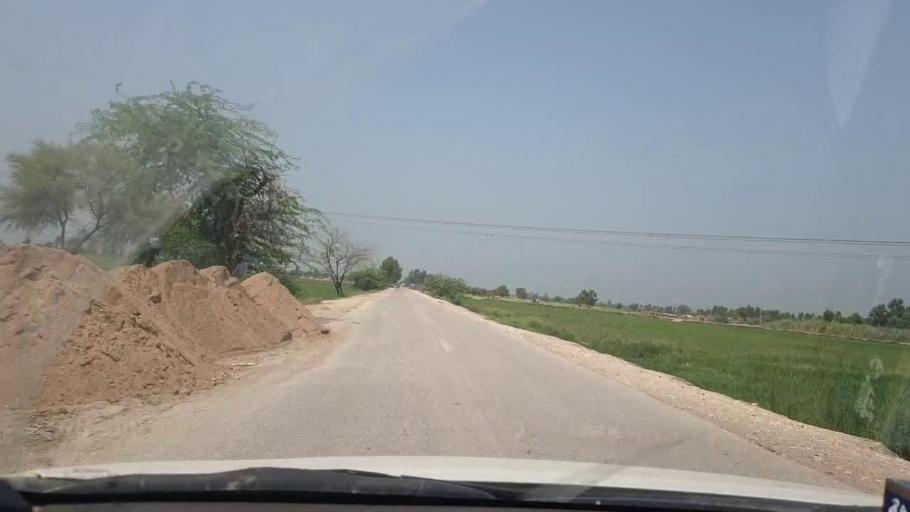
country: PK
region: Sindh
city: Rustam jo Goth
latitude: 27.9558
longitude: 68.7329
